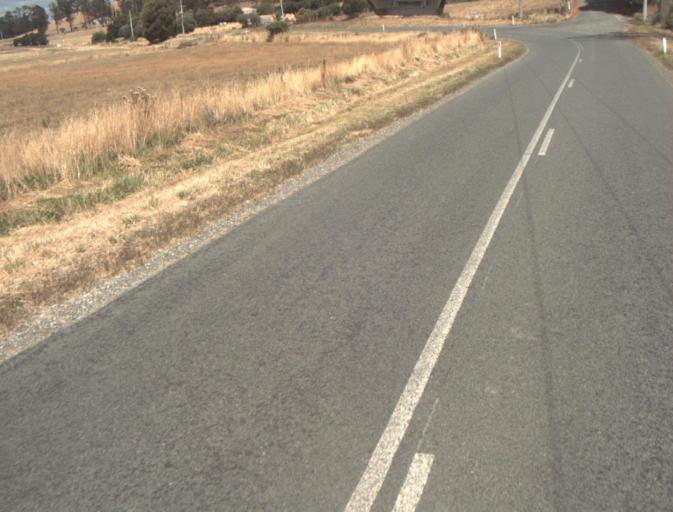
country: AU
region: Tasmania
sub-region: Launceston
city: Mayfield
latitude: -41.2332
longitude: 147.1253
